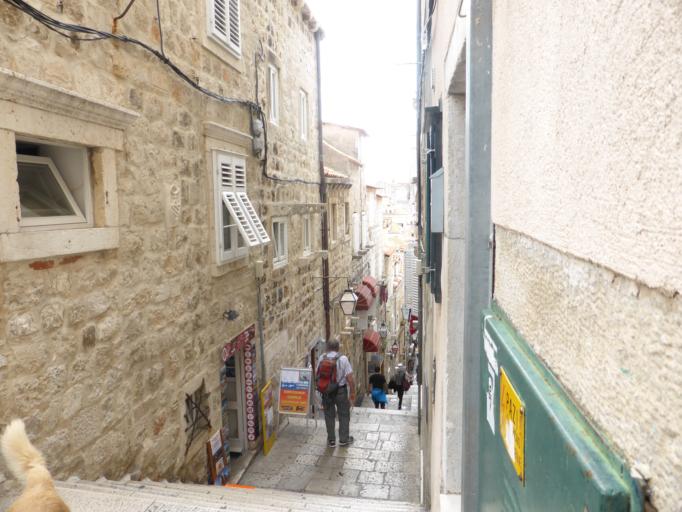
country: HR
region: Dubrovacko-Neretvanska
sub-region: Grad Dubrovnik
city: Dubrovnik
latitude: 42.6431
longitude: 18.1101
